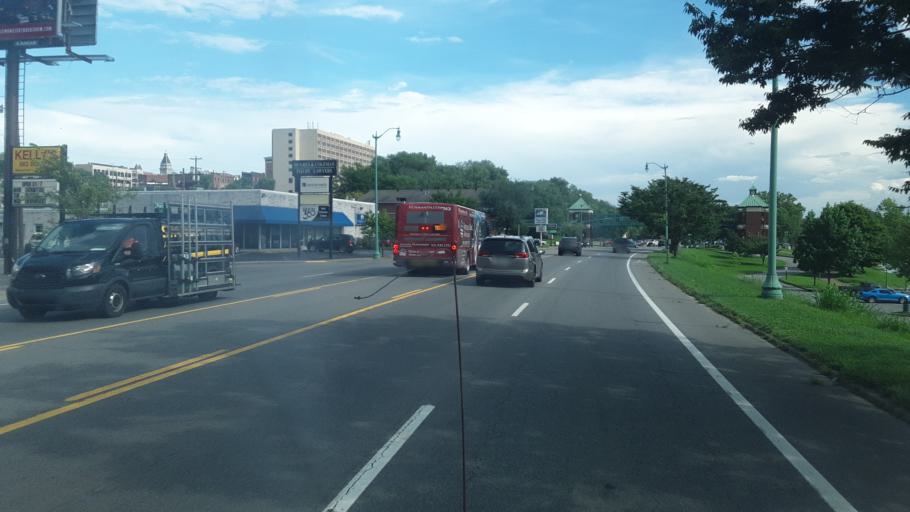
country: US
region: Tennessee
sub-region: Montgomery County
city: Clarksville
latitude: 36.5309
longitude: -87.3645
